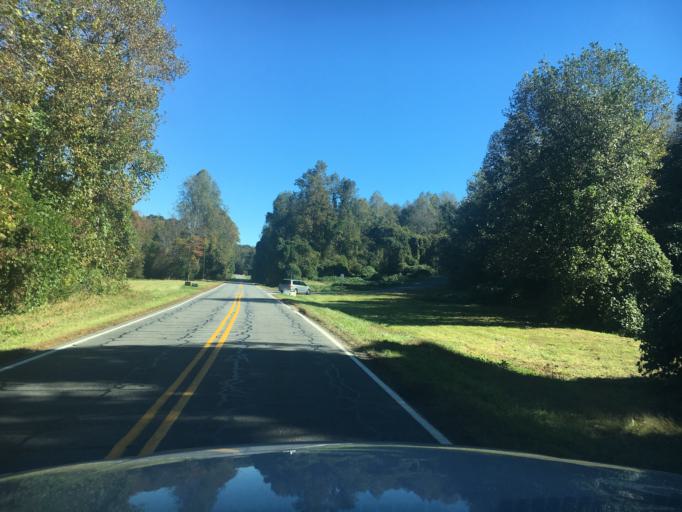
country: US
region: North Carolina
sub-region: Rutherford County
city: Rutherfordton
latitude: 35.3402
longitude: -81.9561
